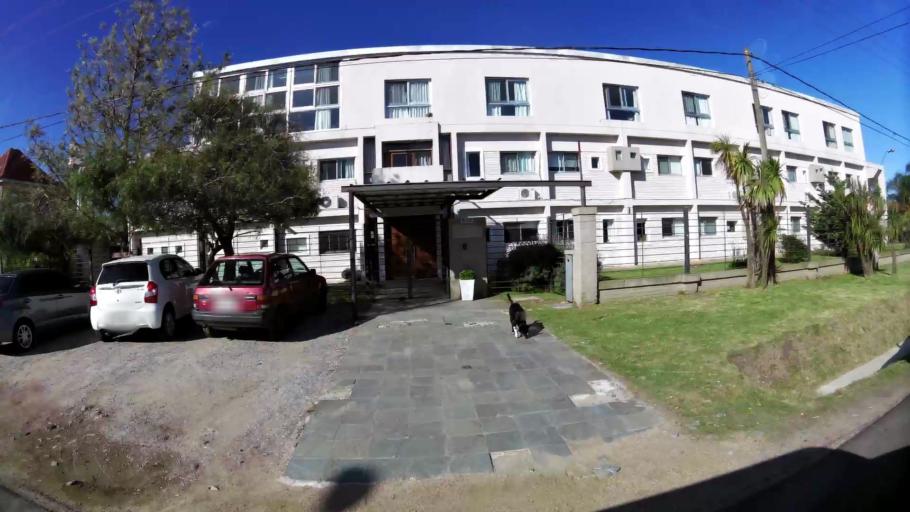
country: UY
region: Canelones
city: Barra de Carrasco
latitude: -34.8718
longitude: -56.0200
